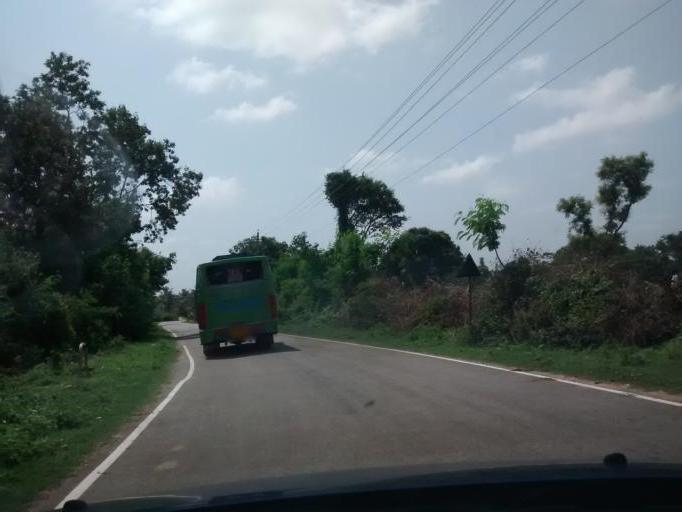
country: IN
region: Karnataka
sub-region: Hassan
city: Konanur
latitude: 12.6545
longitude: 76.1830
